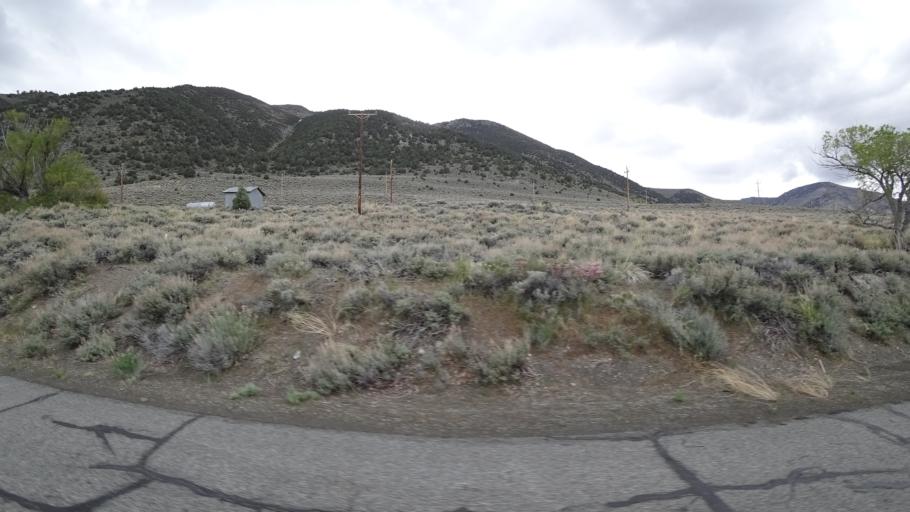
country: US
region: California
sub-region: Mono County
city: Bridgeport
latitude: 38.0096
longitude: -119.1549
